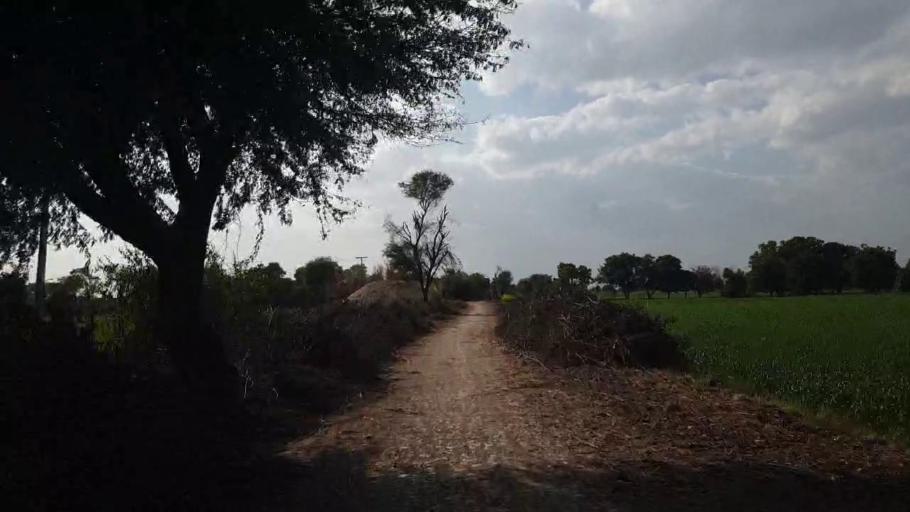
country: PK
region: Sindh
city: Shahdadpur
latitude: 26.0253
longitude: 68.4774
